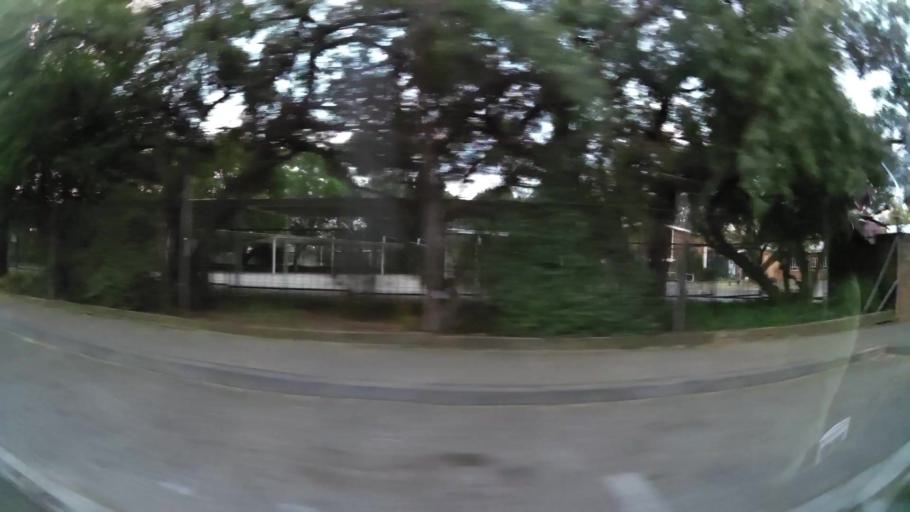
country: ZA
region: Gauteng
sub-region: Ekurhuleni Metropolitan Municipality
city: Benoni
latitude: -26.1756
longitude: 28.3080
